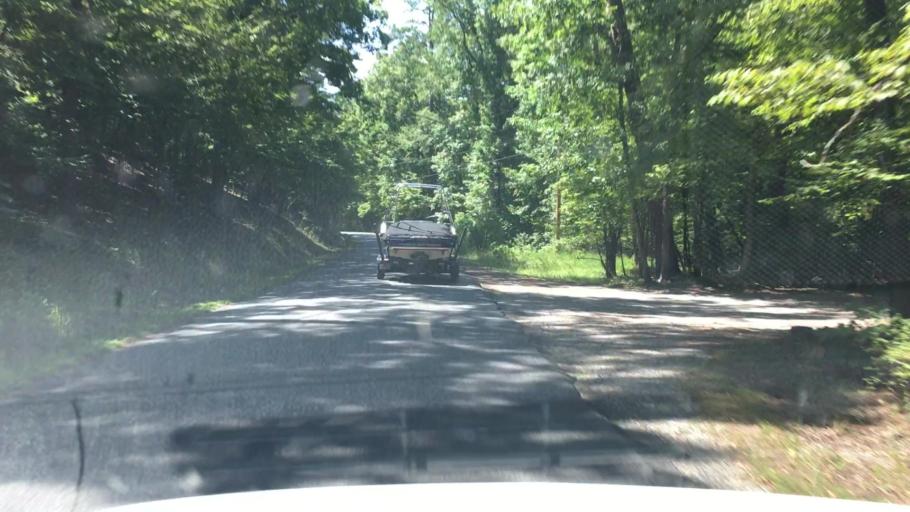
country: US
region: Arkansas
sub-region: Garland County
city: Piney
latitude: 34.5392
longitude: -93.3426
